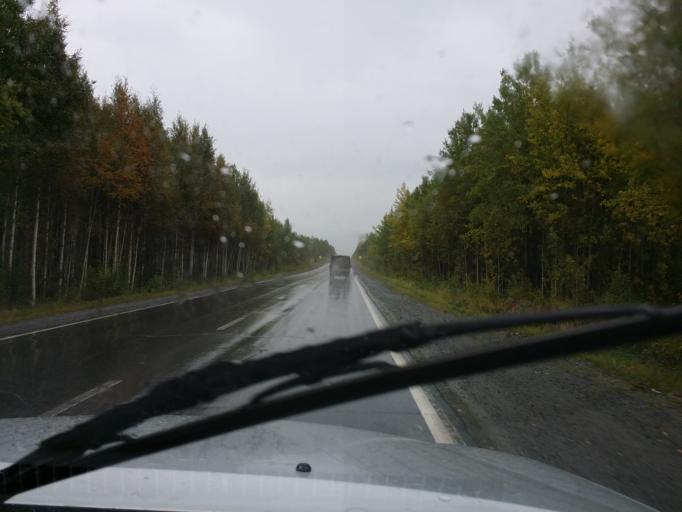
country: RU
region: Khanty-Mansiyskiy Avtonomnyy Okrug
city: Langepas
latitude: 61.1589
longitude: 75.6277
